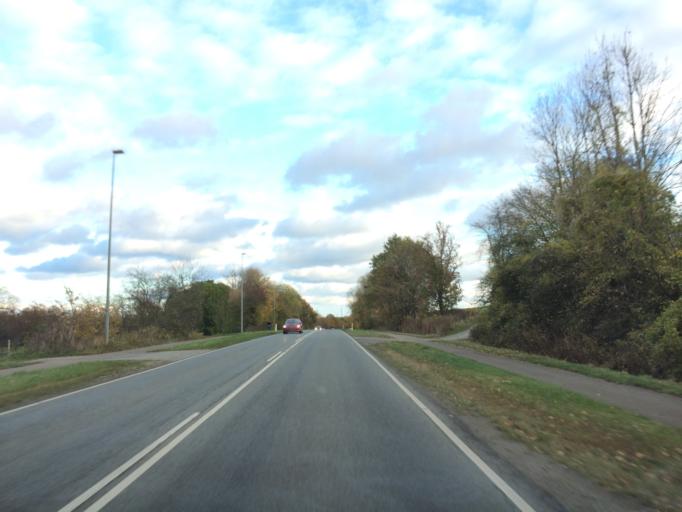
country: DK
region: South Denmark
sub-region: Sonderborg Kommune
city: Nordborg
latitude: 55.0410
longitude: 9.8000
